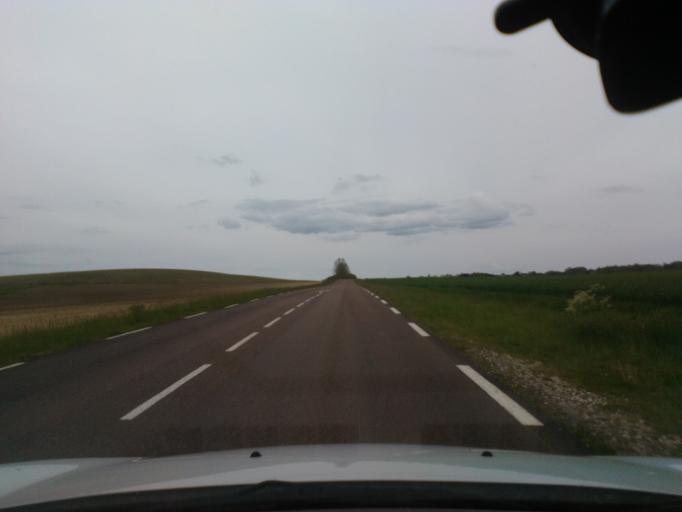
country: FR
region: Champagne-Ardenne
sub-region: Departement de l'Aube
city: Bar-sur-Aube
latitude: 48.2250
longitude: 4.7781
